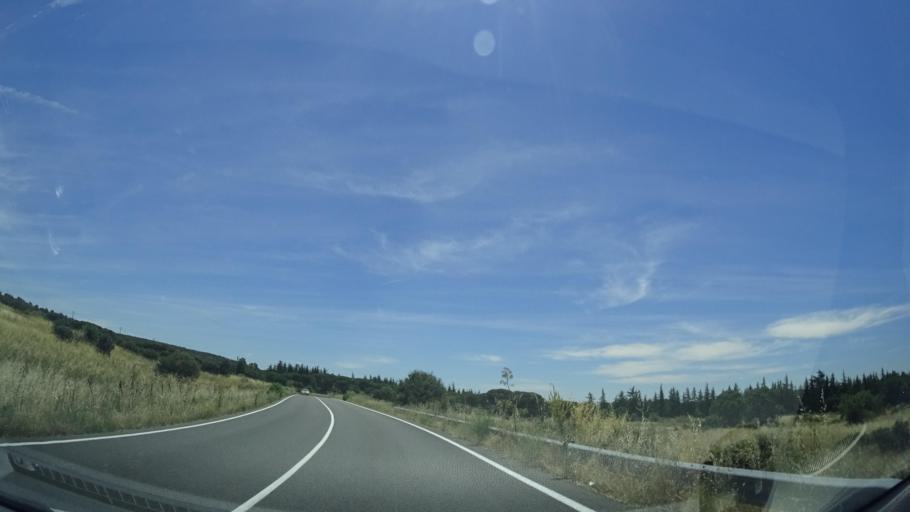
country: ES
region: Madrid
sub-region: Provincia de Madrid
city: Collado-Villalba
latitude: 40.6085
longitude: -3.9794
